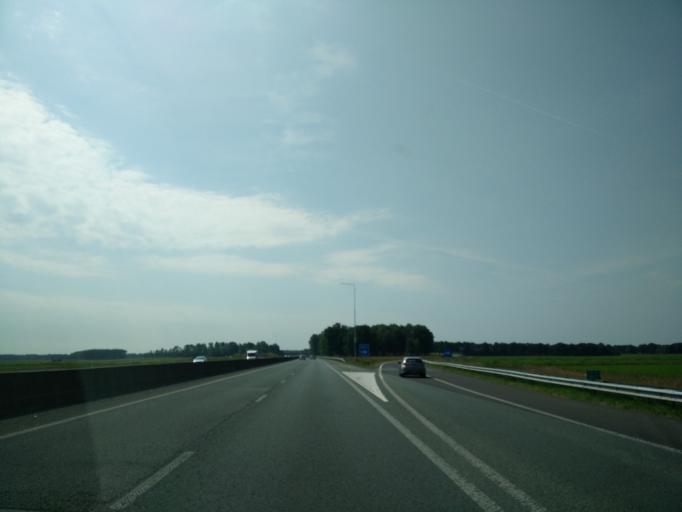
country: NL
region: Drenthe
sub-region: Gemeente Tynaarlo
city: Tynaarlo
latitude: 53.1172
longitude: 6.6105
